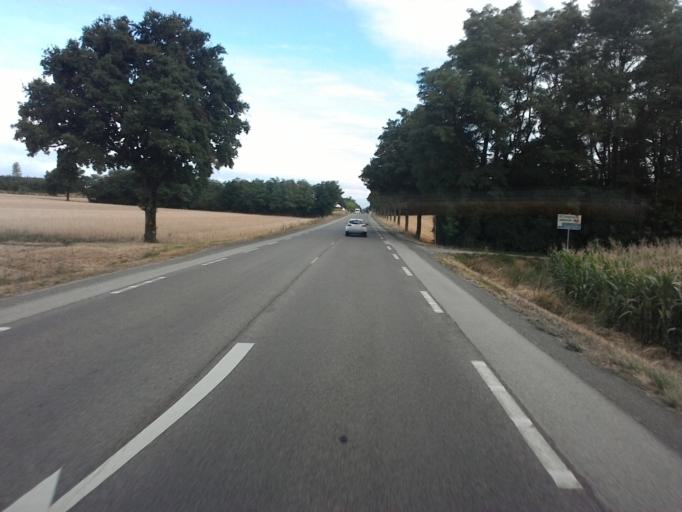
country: FR
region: Rhone-Alpes
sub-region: Departement de l'Ain
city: Tossiat
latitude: 46.1270
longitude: 5.2928
